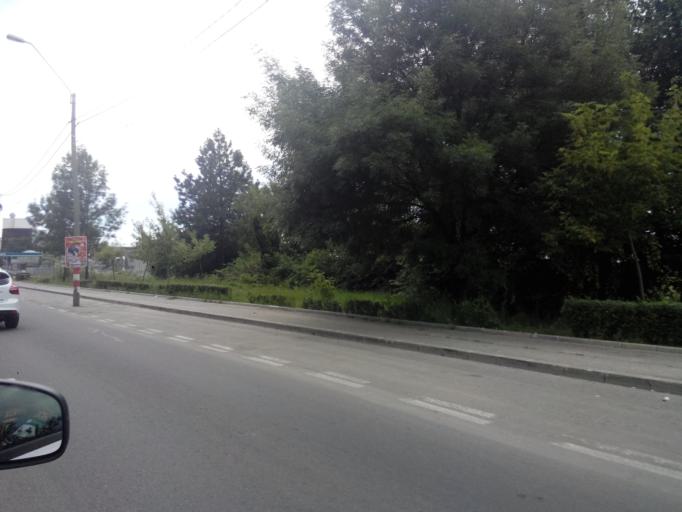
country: RO
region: Arges
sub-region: Comuna Bascov
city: Bascov
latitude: 44.8812
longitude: 24.8357
